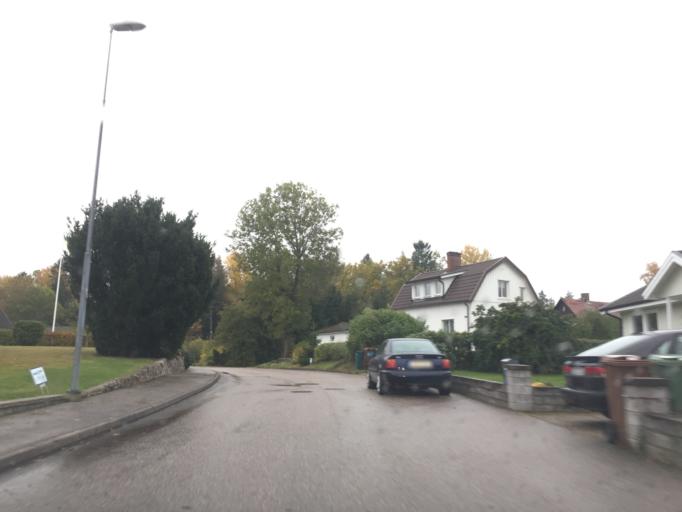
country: SE
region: Vaestra Goetaland
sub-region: Trollhattan
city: Trollhattan
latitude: 58.2860
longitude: 12.3388
